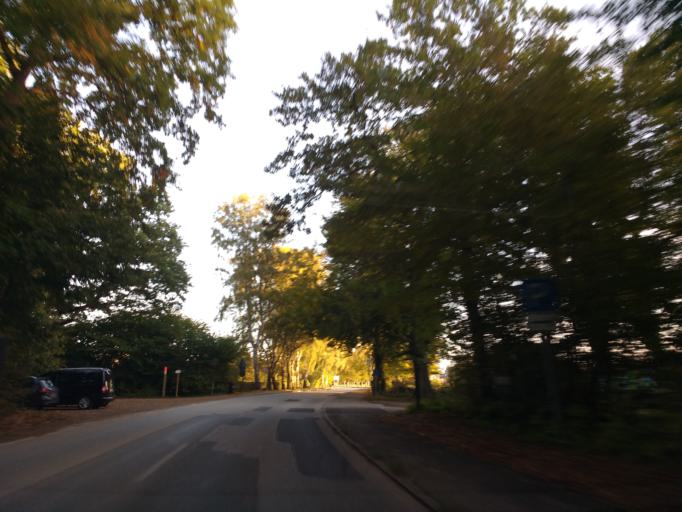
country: DE
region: Schleswig-Holstein
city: Kellenhusen
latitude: 54.1950
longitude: 11.0519
